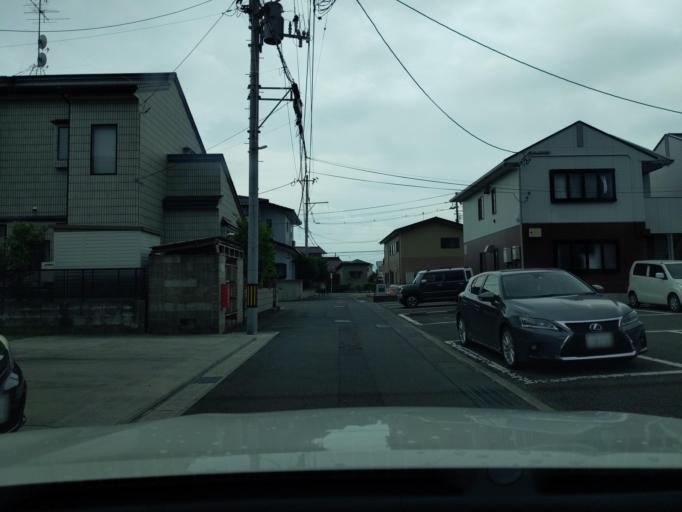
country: JP
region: Fukushima
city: Koriyama
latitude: 37.4158
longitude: 140.3533
